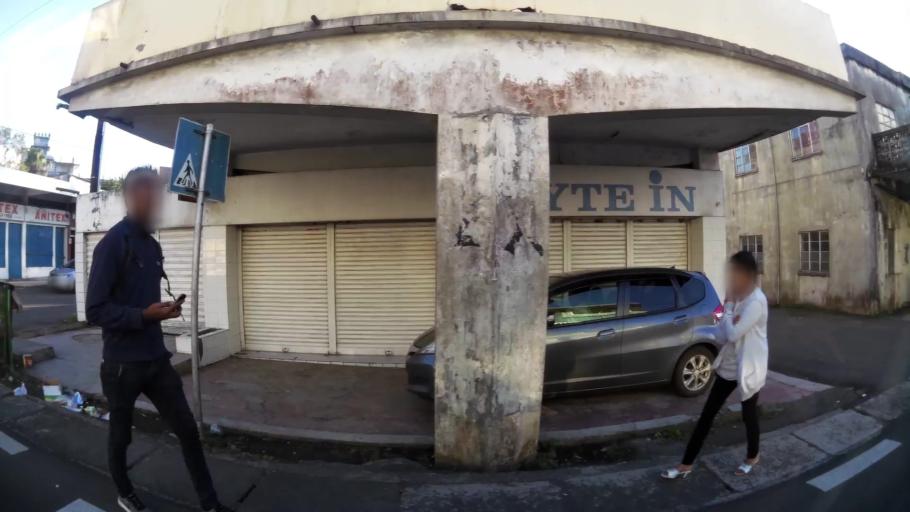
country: MU
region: Plaines Wilhems
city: Curepipe
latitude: -20.3129
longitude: 57.5238
